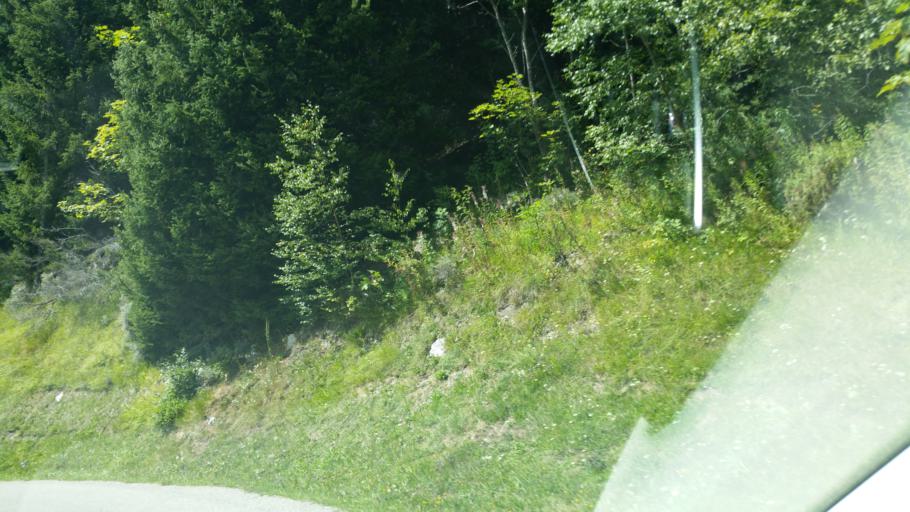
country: FR
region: Rhone-Alpes
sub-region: Departement de la Savoie
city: La Chambre
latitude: 45.4163
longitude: 6.3438
